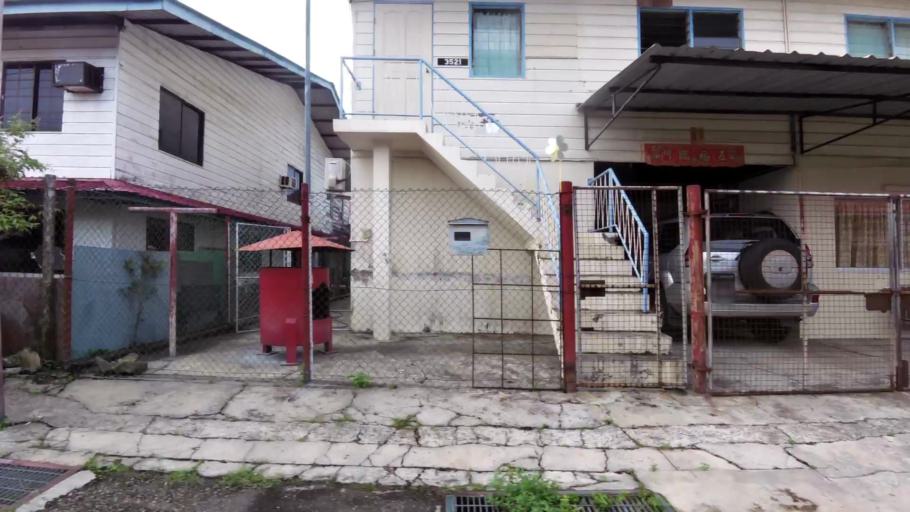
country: BN
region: Belait
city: Seria
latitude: 4.6155
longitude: 114.3479
